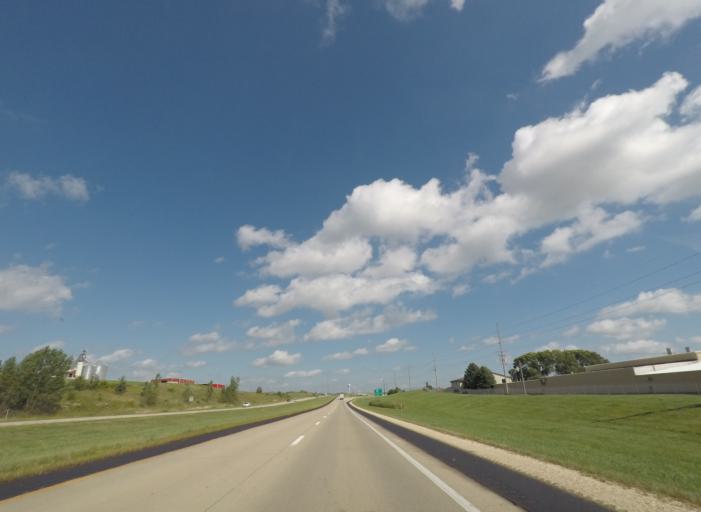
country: US
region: Iowa
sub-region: Dubuque County
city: Cascade
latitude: 42.3106
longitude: -91.0073
